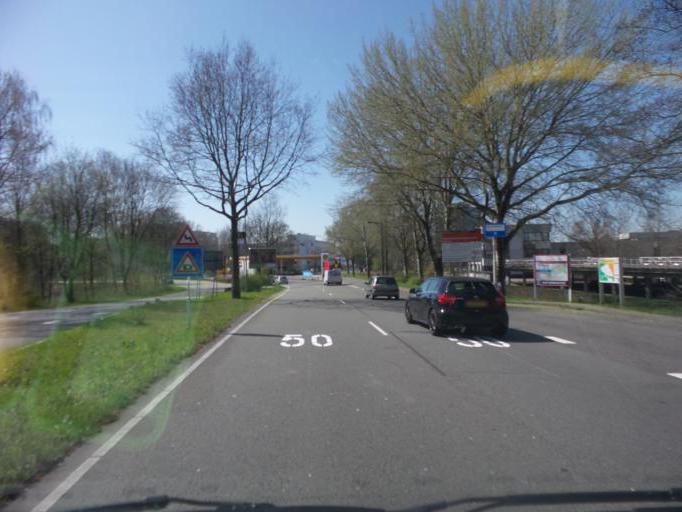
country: NL
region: South Holland
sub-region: Gemeente Gouda
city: Bloemendaal
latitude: 52.0259
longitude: 4.6825
